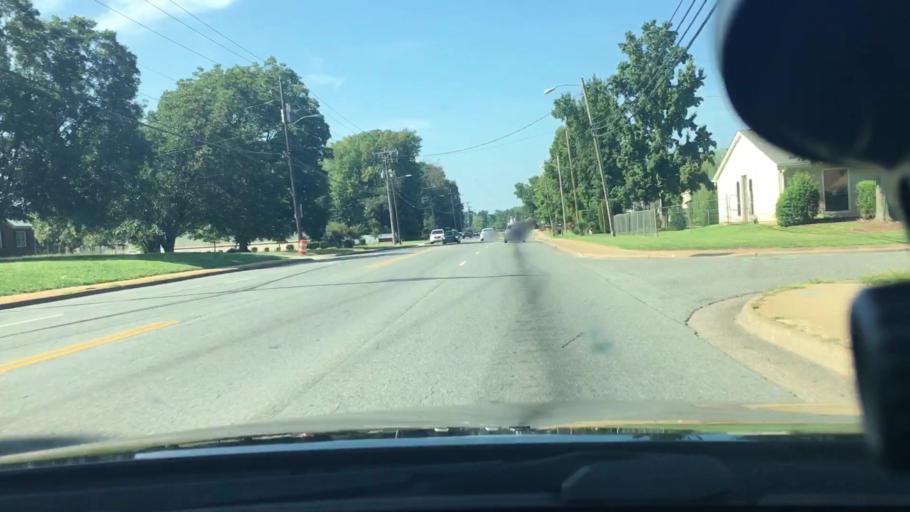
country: US
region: North Carolina
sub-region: Mecklenburg County
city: Matthews
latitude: 35.1902
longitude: -80.7278
